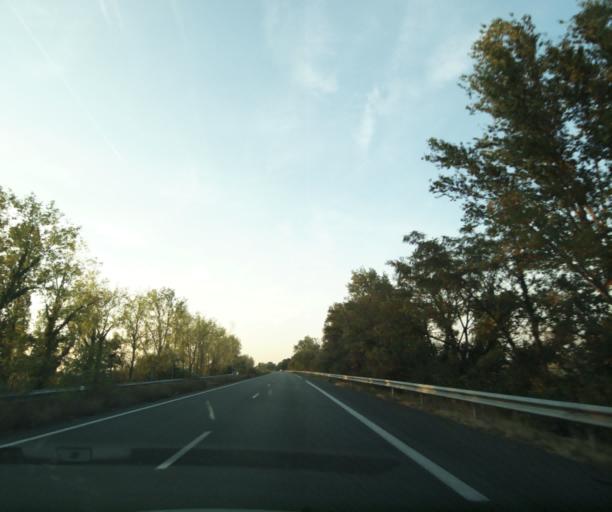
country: FR
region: Aquitaine
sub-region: Departement du Lot-et-Garonne
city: Tonneins
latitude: 44.3593
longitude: 0.2471
